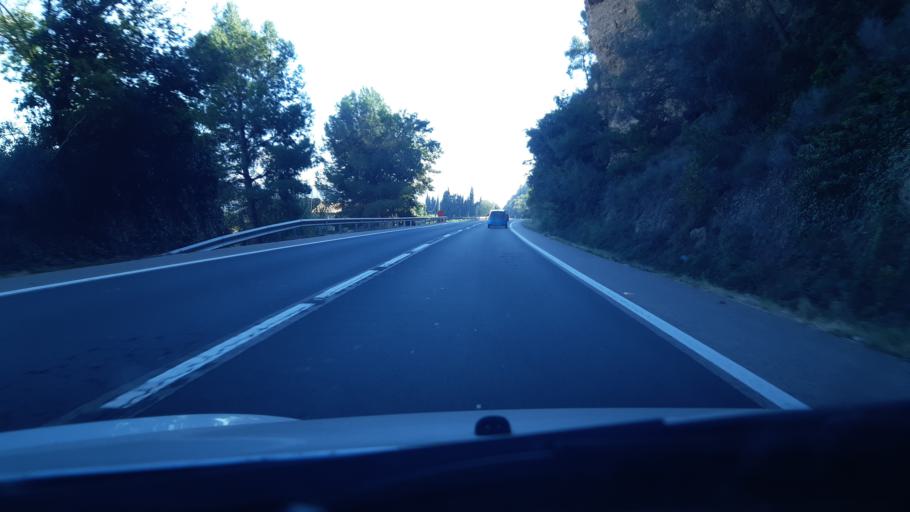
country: ES
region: Catalonia
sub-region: Provincia de Tarragona
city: Tivenys
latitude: 40.8683
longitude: 0.5036
